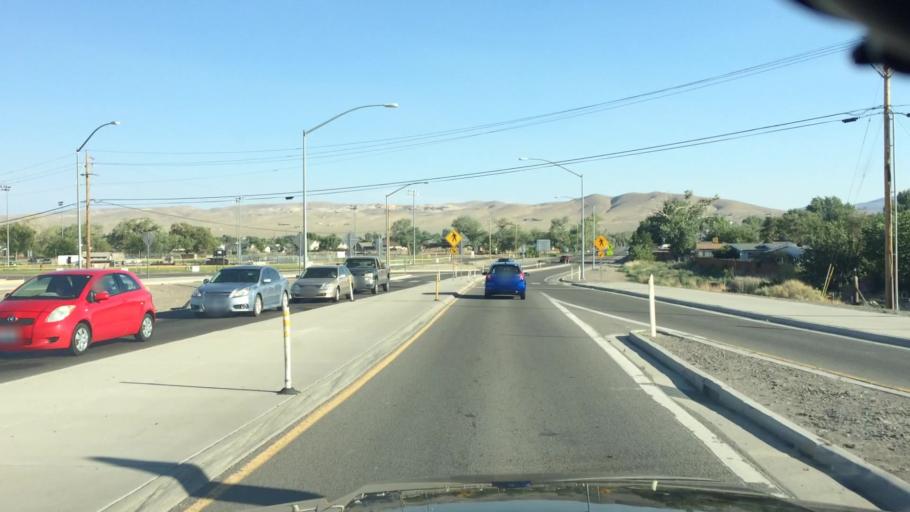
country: US
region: Nevada
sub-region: Lyon County
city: Fernley
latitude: 39.6032
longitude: -119.2271
